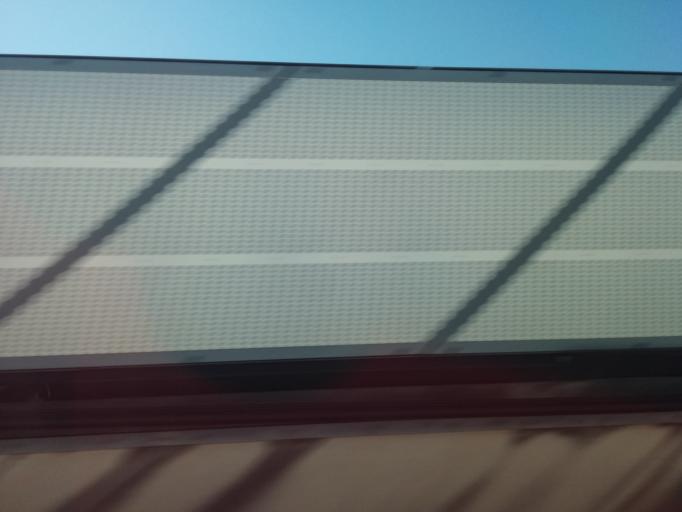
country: JP
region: Aichi
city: Chiryu
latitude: 34.9868
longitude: 137.0428
